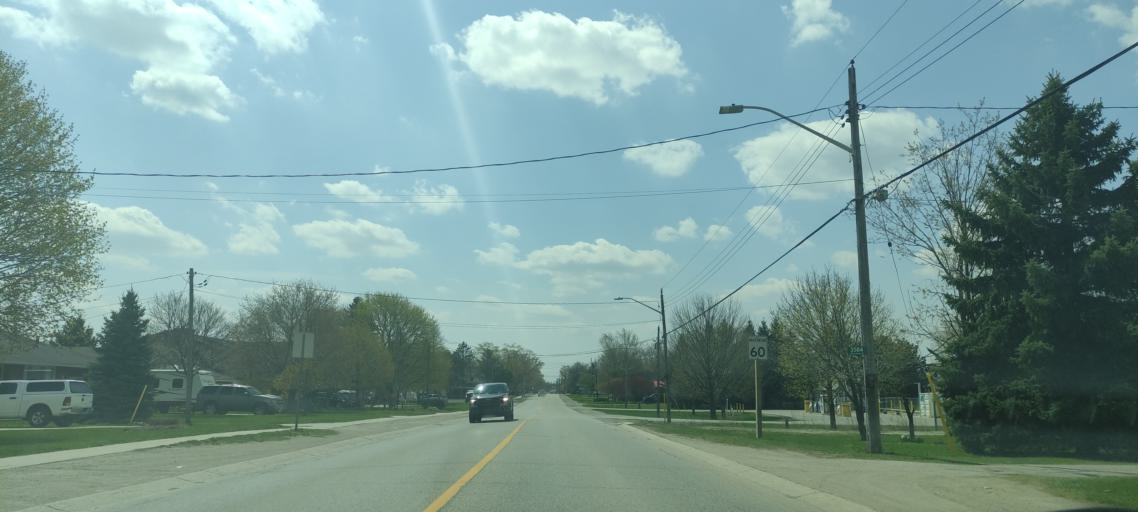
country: CA
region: Ontario
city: Stratford
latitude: 43.3312
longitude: -80.8363
